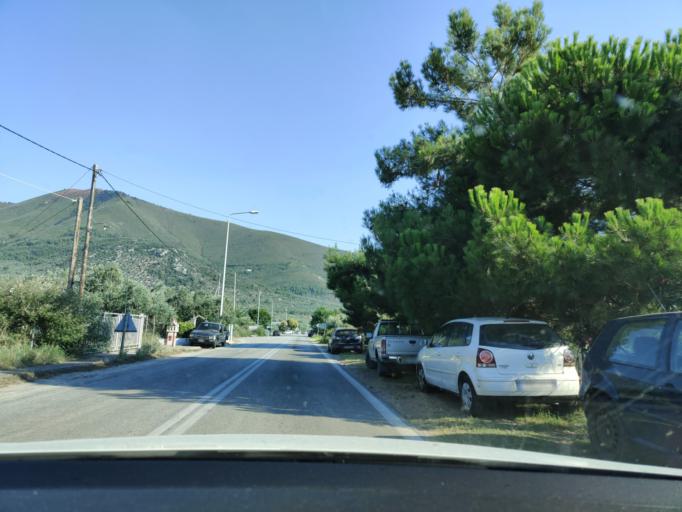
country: GR
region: East Macedonia and Thrace
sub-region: Nomos Kavalas
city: Prinos
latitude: 40.6936
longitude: 24.5256
